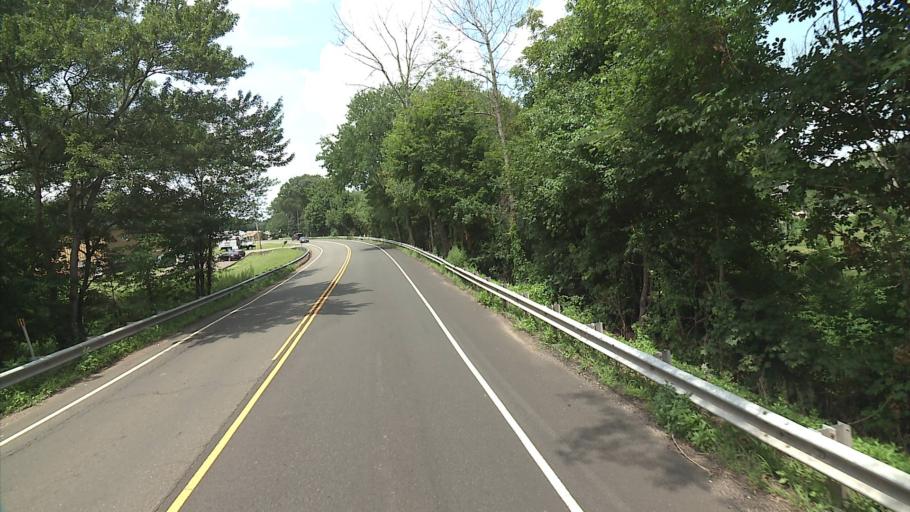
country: US
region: Connecticut
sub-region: New Haven County
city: North Haven
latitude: 41.3807
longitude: -72.8107
